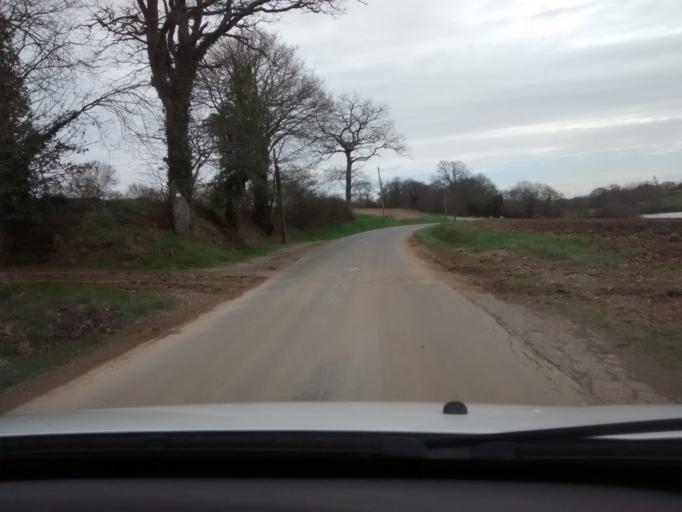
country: FR
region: Brittany
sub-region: Departement d'Ille-et-Vilaine
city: La Bouexiere
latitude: 48.1956
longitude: -1.4602
